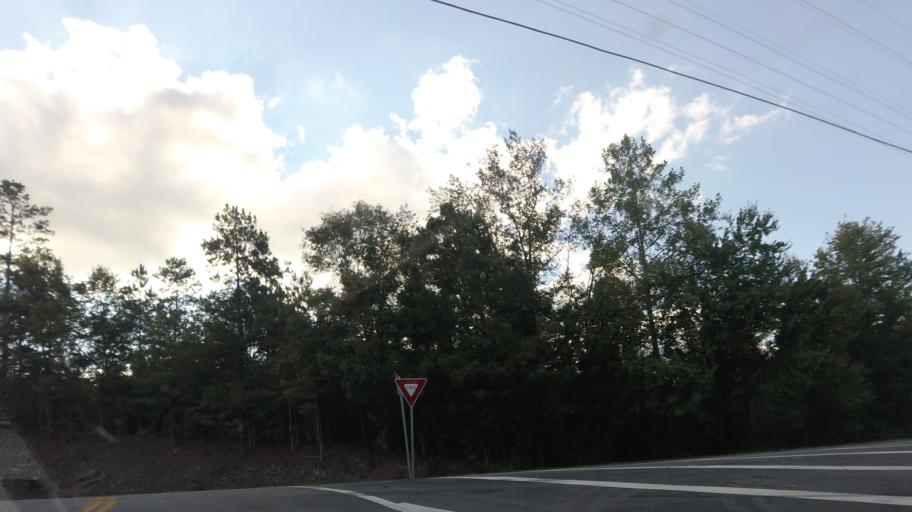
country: US
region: Georgia
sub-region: Lamar County
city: Barnesville
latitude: 33.0858
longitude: -84.1546
